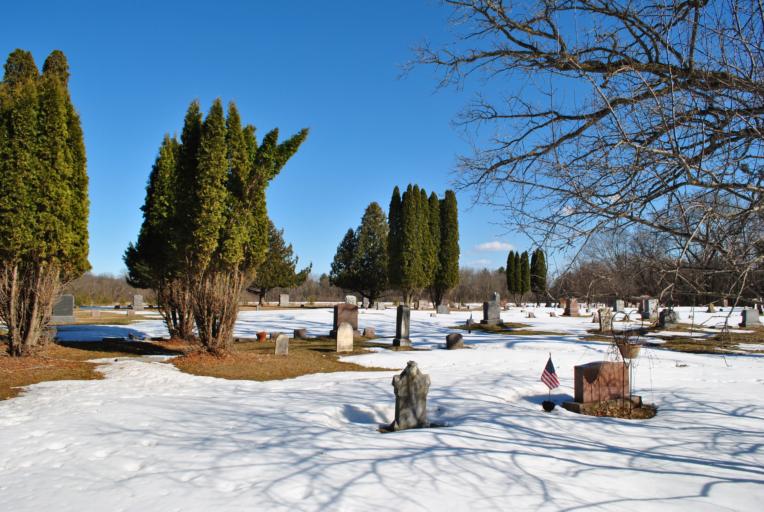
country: US
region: Wisconsin
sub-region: Dunn County
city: Menomonie
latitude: 44.7743
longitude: -91.9223
